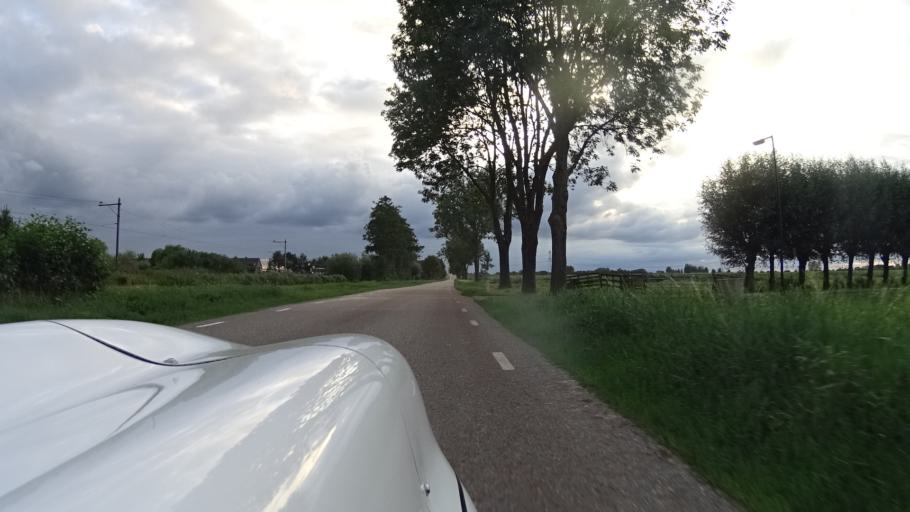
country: NL
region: South Holland
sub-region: Gemeente Hardinxveld-Giessendam
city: Neder-Hardinxveld
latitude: 51.8302
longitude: 4.8184
